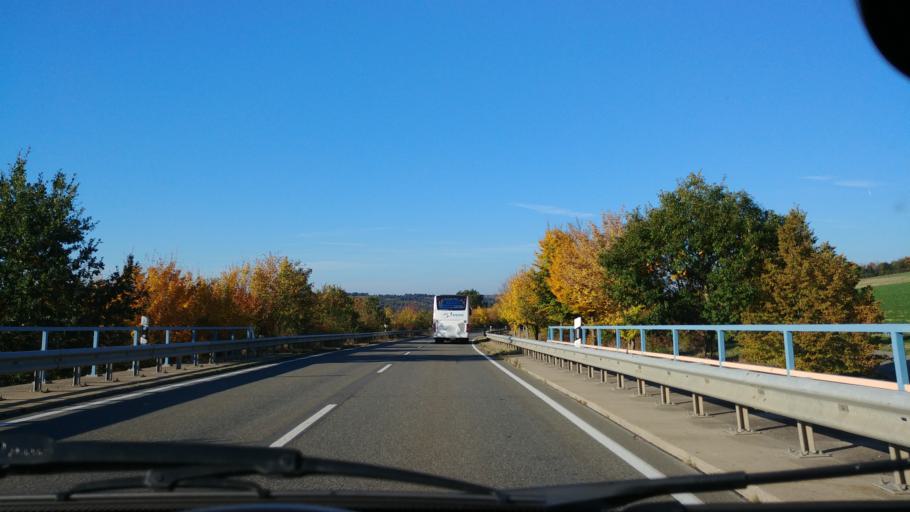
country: DE
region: Rheinland-Pfalz
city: Buch
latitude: 50.1948
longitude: 7.8862
